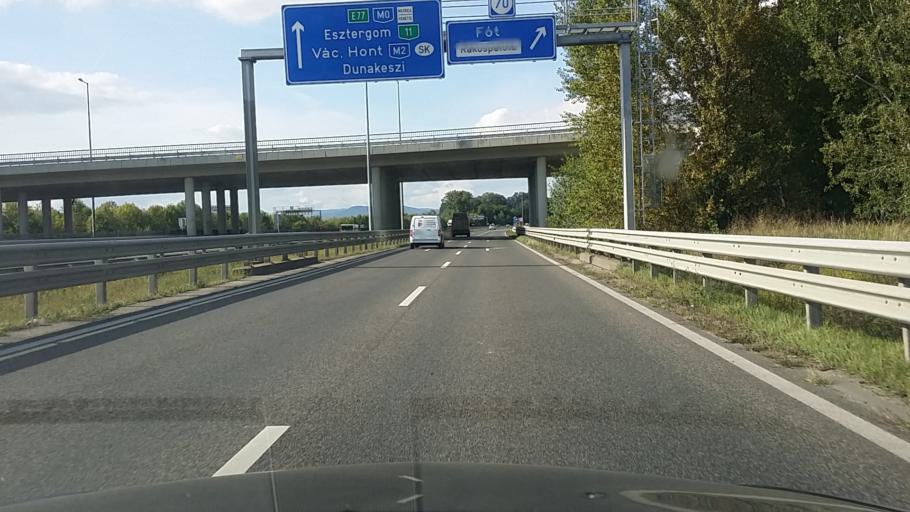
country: HU
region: Budapest
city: Budapest XV. keruelet
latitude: 47.5804
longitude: 19.1503
